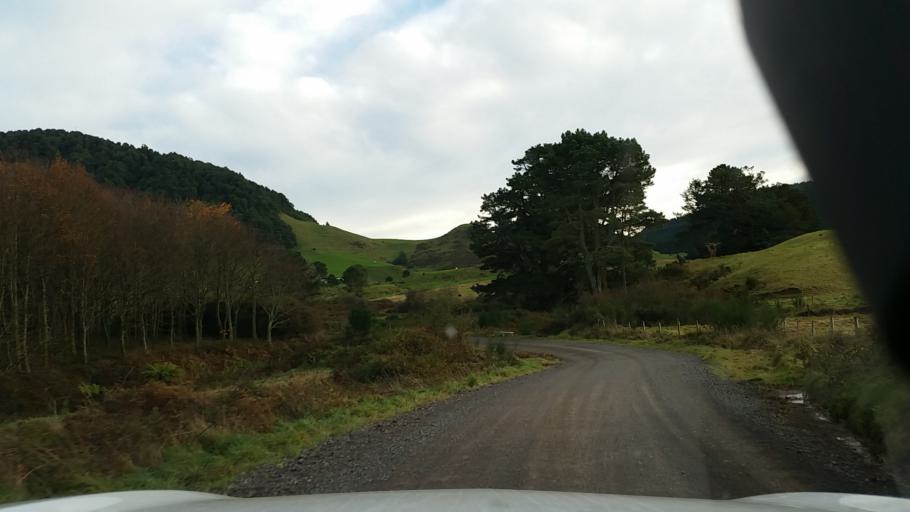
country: NZ
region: Bay of Plenty
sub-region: Rotorua District
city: Rotorua
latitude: -38.2355
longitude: 176.1653
